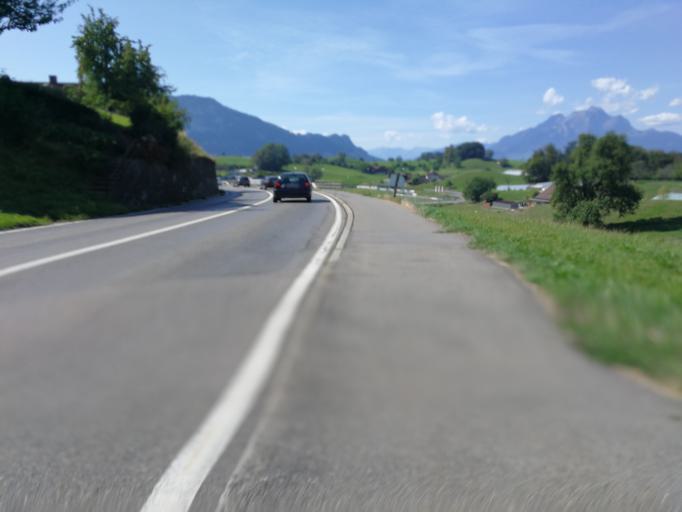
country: CH
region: Lucerne
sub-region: Lucerne-Land District
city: Weggis
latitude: 47.0405
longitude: 8.4227
